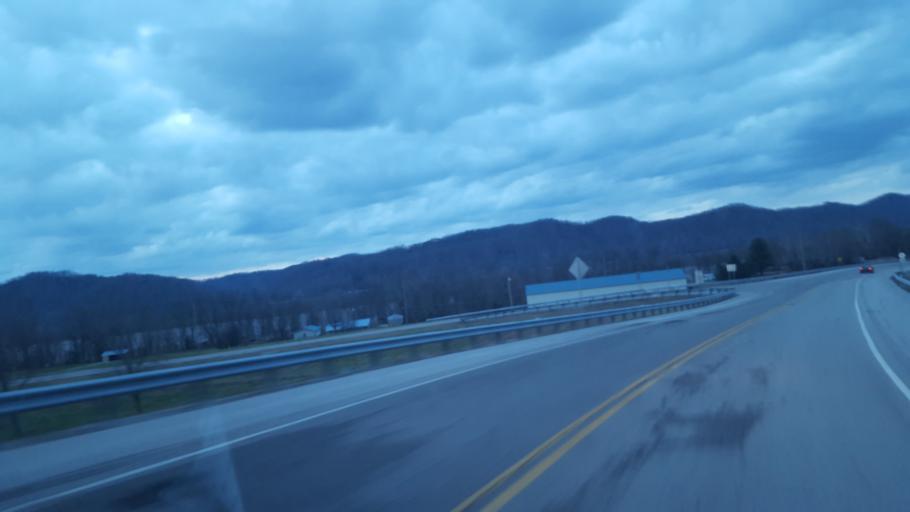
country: US
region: Kentucky
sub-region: Lewis County
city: Vanceburg
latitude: 38.6151
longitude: -83.1431
